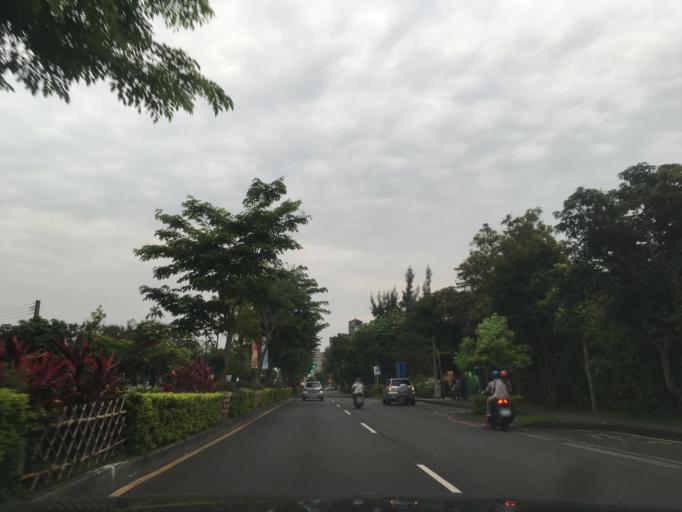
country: TW
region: Taiwan
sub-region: Yilan
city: Yilan
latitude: 24.7536
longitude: 121.7572
